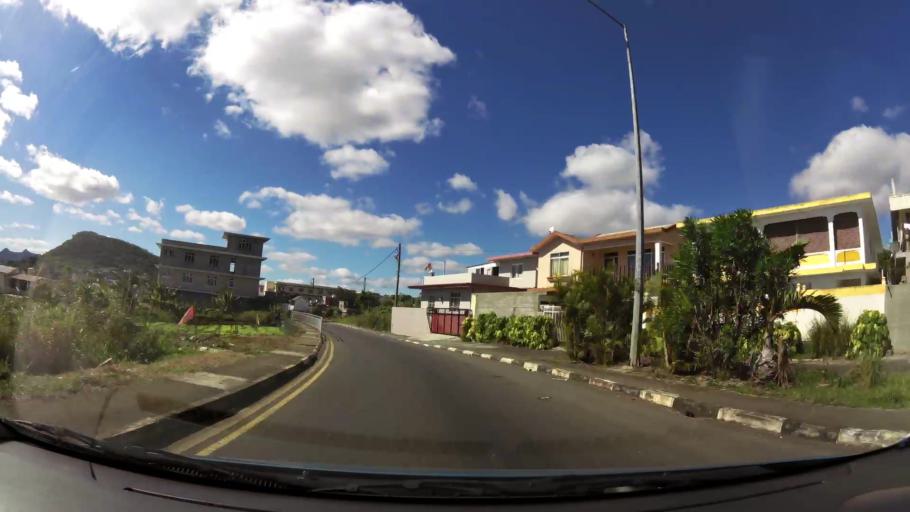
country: MU
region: Plaines Wilhems
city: Vacoas
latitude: -20.2867
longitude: 57.4771
